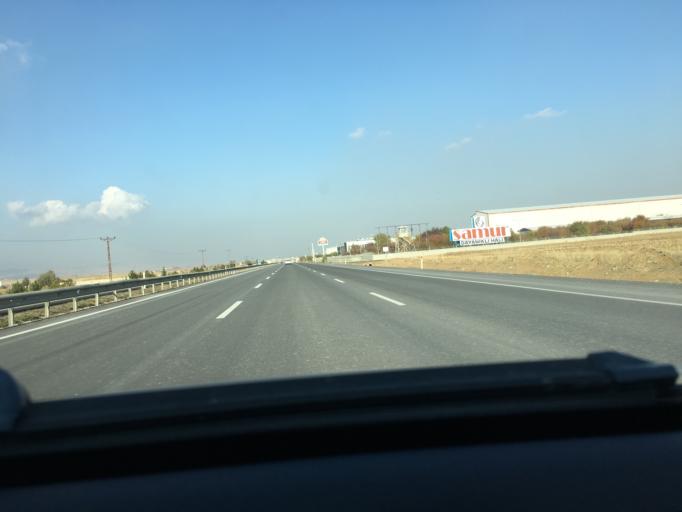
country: TR
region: Ankara
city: Polatli
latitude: 39.6433
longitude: 32.2073
